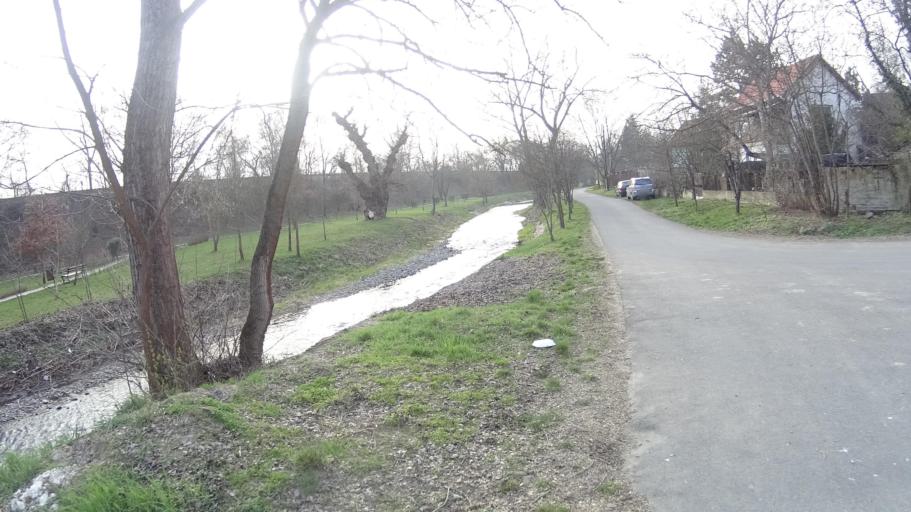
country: HU
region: Pest
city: Veroce
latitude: 47.8261
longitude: 19.0183
